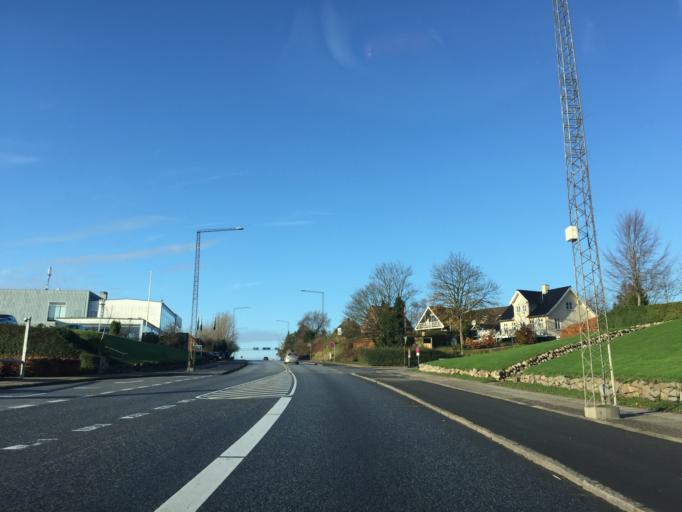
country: DK
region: Central Jutland
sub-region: Arhus Kommune
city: Arhus
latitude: 56.1691
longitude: 10.1613
